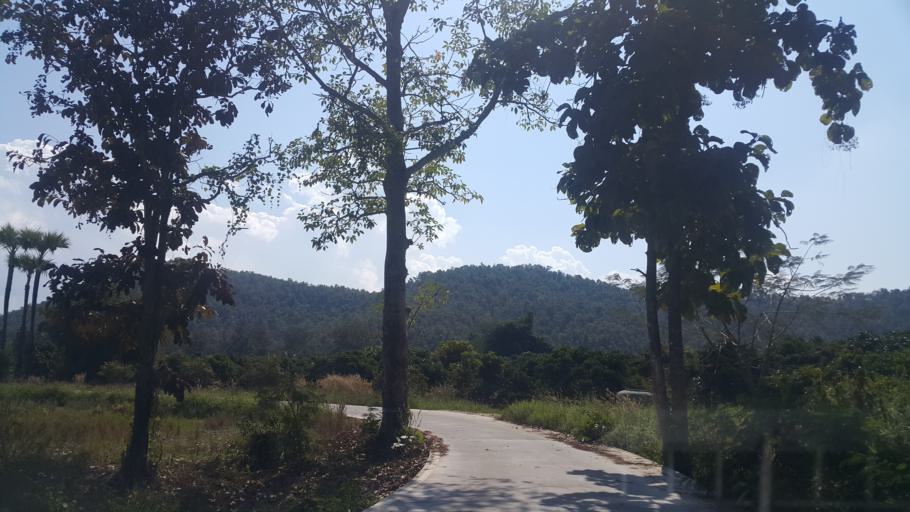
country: TH
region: Lamphun
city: Ban Thi
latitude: 18.6803
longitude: 99.1665
